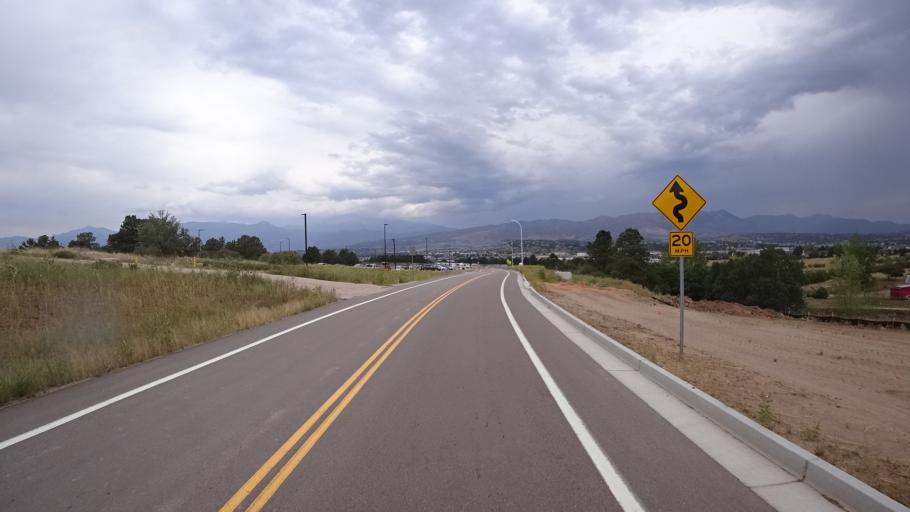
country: US
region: Colorado
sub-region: El Paso County
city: Colorado Springs
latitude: 38.8999
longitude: -104.8089
